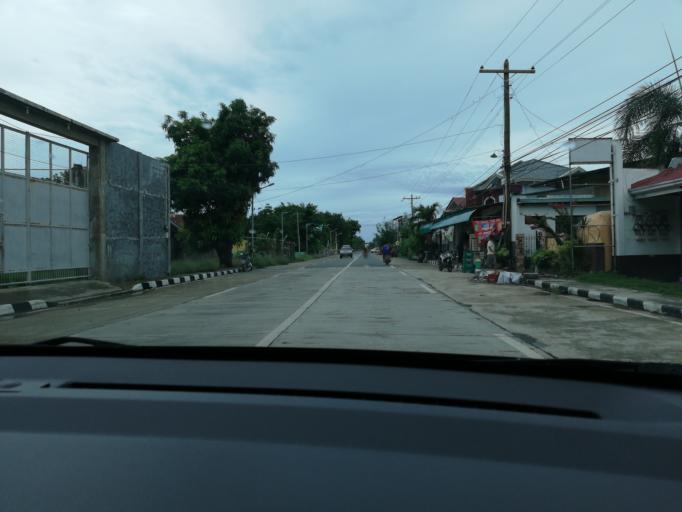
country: PH
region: Ilocos
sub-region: Province of Ilocos Sur
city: San Vicente
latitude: 17.5842
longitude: 120.3720
